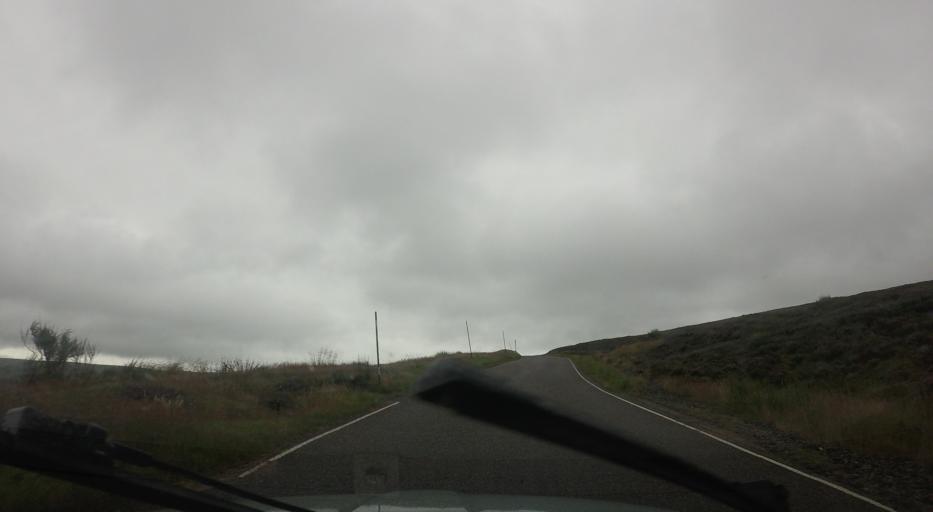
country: GB
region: Scotland
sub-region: Aberdeenshire
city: Banchory
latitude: 56.9353
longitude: -2.5715
